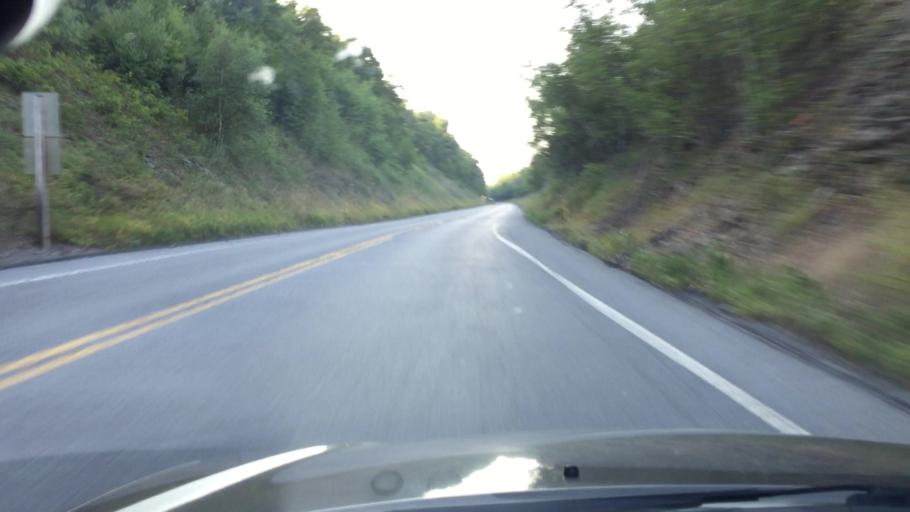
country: US
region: Pennsylvania
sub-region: Carbon County
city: Nesquehoning
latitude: 40.8815
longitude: -75.7994
